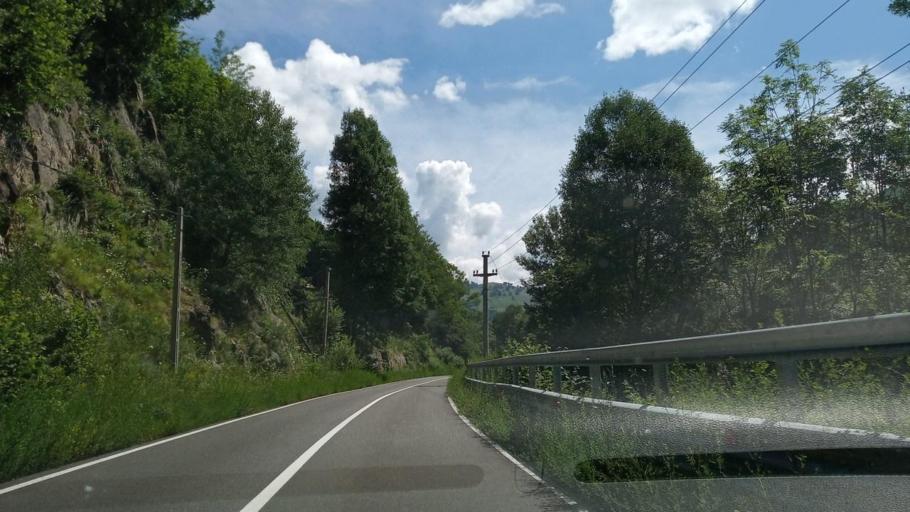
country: RO
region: Alba
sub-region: Comuna Sugag
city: Sugag
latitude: 45.6858
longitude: 23.5995
